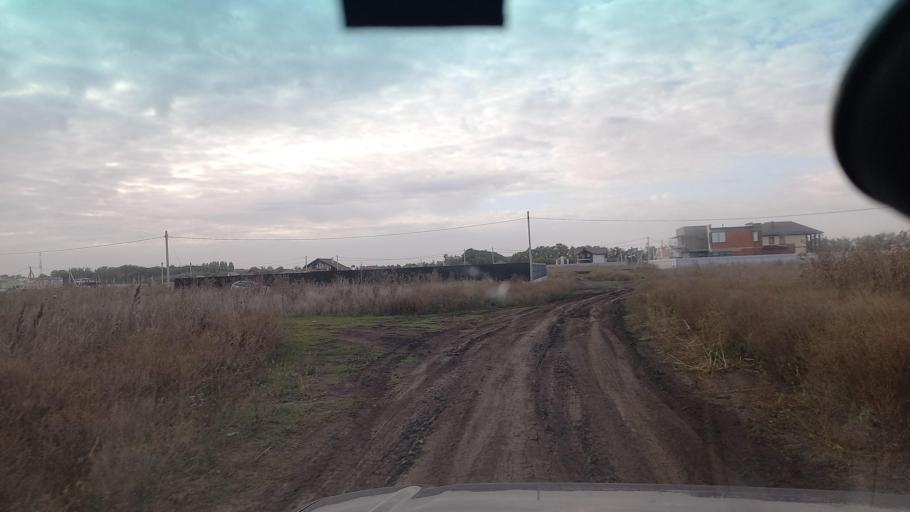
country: RU
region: Krasnodarskiy
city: Krasnodar
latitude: 45.1349
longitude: 38.9209
